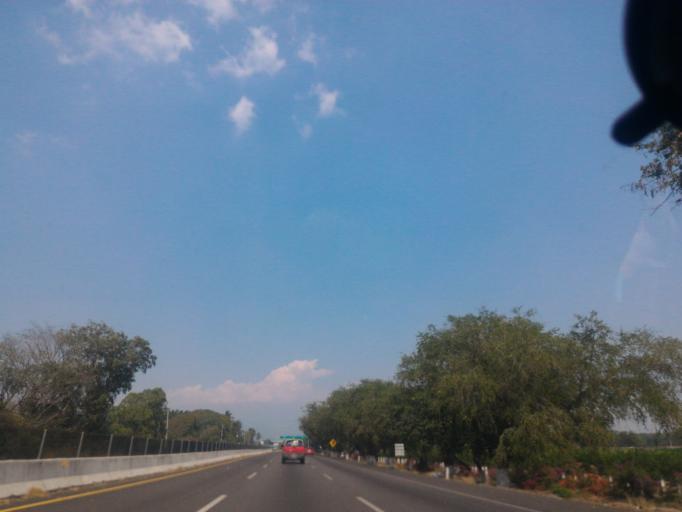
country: MX
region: Colima
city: Colima
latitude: 19.2009
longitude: -103.7452
